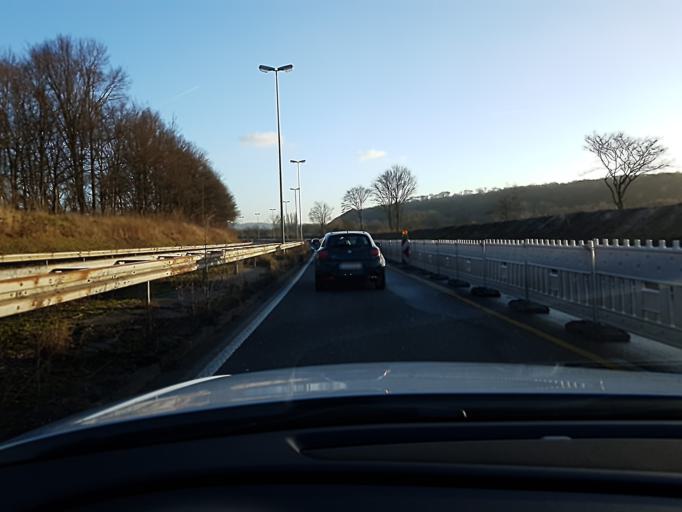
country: DE
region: North Rhine-Westphalia
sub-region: Regierungsbezirk Dusseldorf
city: Essen
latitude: 51.4261
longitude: 7.0603
